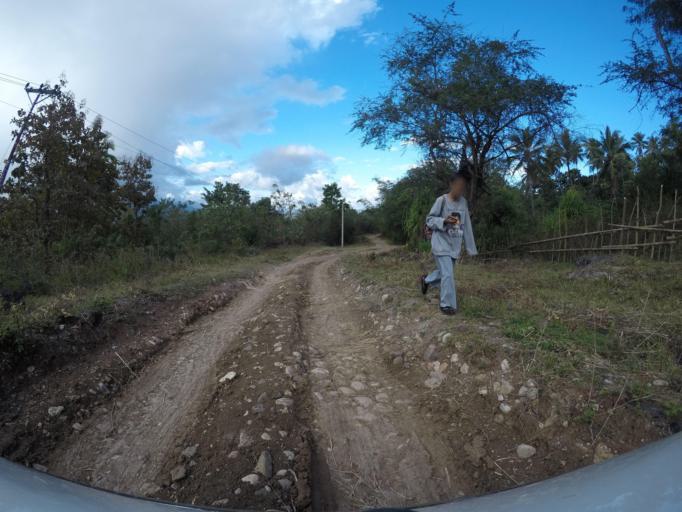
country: TL
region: Baucau
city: Venilale
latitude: -8.6879
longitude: 126.6659
